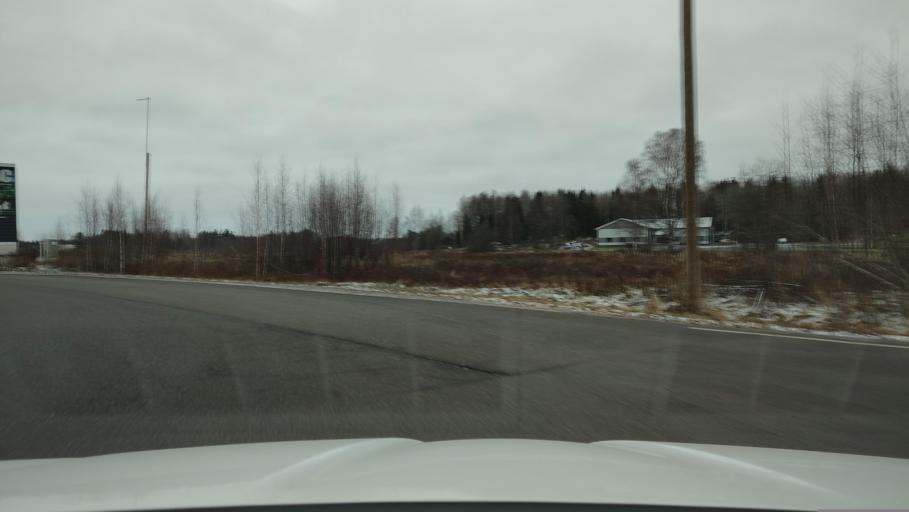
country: FI
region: Ostrobothnia
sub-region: Vaasa
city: Ristinummi
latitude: 63.0367
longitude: 21.7821
